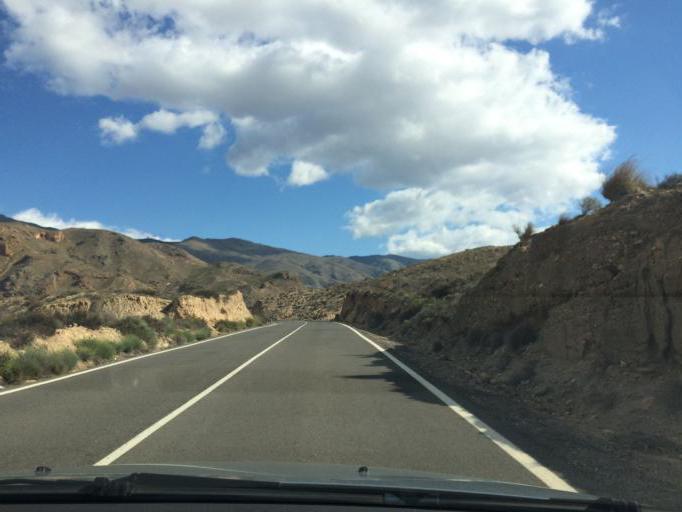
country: ES
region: Andalusia
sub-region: Provincia de Almeria
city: Pechina
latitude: 36.9442
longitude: -2.4226
